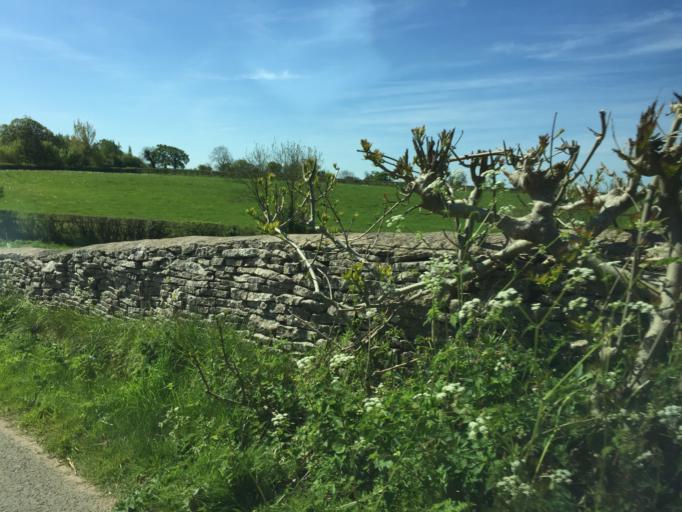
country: GB
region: England
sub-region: Wiltshire
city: Luckington
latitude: 51.6075
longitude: -2.2588
